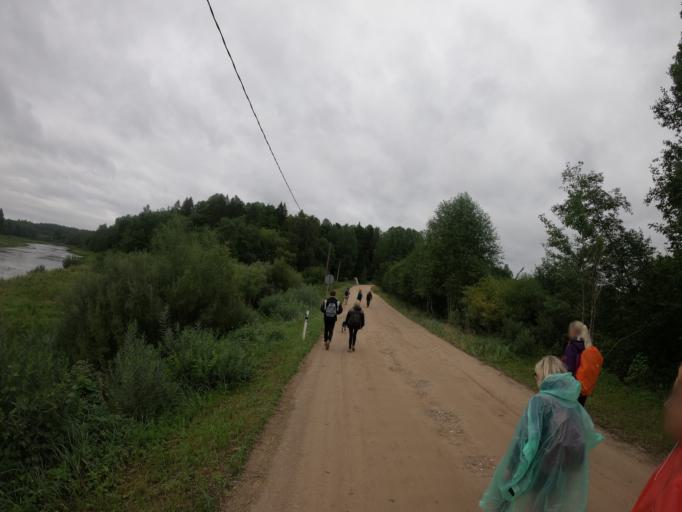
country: LV
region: Kuldigas Rajons
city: Kuldiga
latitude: 57.0085
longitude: 21.9789
